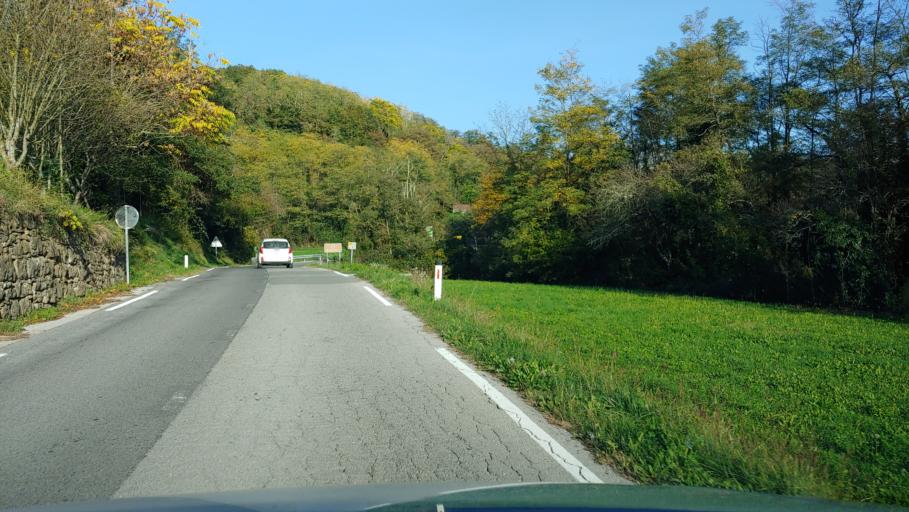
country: SI
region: Vipava
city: Vipava
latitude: 45.8142
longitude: 13.9004
